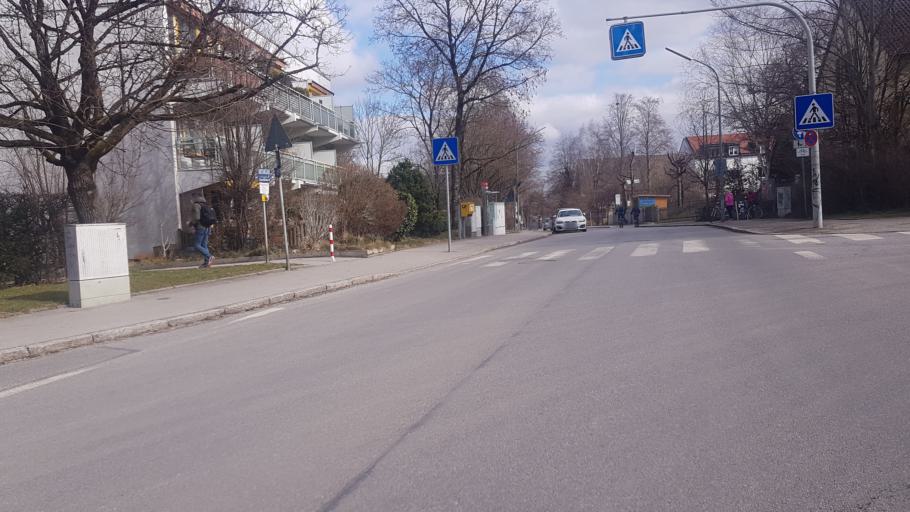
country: DE
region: Bavaria
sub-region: Upper Bavaria
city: Unterfoehring
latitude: 48.1694
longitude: 11.6466
